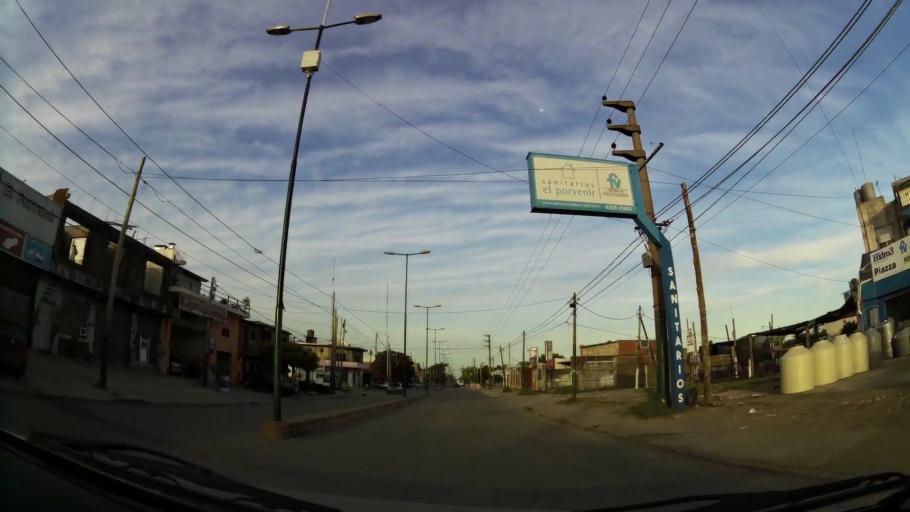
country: AR
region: Buenos Aires
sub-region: Partido de Almirante Brown
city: Adrogue
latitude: -34.7843
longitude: -58.3437
